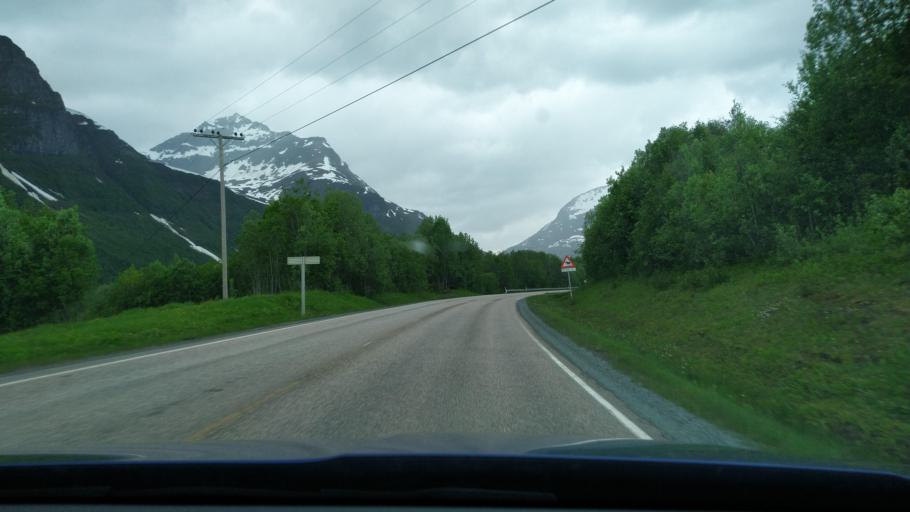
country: NO
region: Troms
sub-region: Balsfjord
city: Storsteinnes
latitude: 69.3786
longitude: 19.2848
